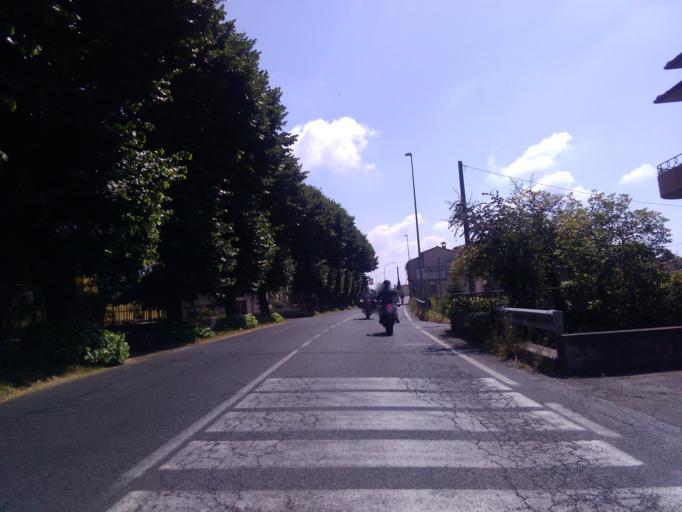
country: IT
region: Tuscany
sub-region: Provincia di Lucca
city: Lucca
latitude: 43.8572
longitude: 10.4338
